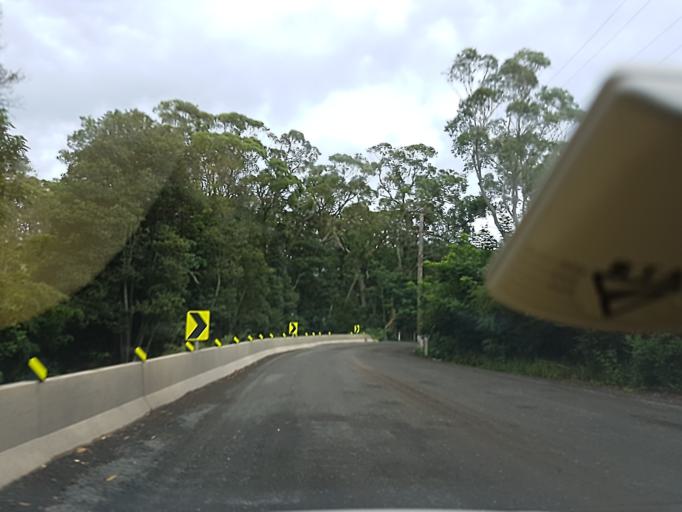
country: AU
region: New South Wales
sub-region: Warringah
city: Davidson
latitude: -33.7288
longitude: 151.2341
